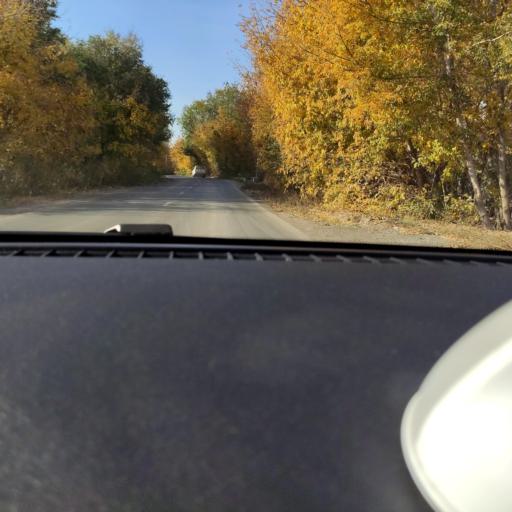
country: RU
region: Samara
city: Smyshlyayevka
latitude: 53.2421
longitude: 50.3538
